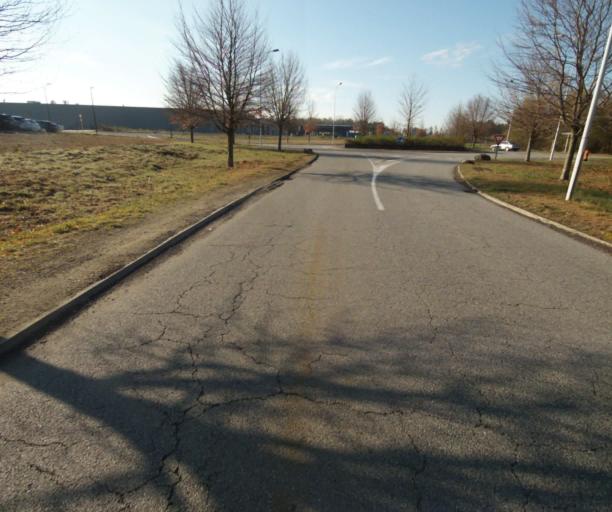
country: FR
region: Limousin
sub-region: Departement de la Correze
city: Correze
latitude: 45.3341
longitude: 1.9012
